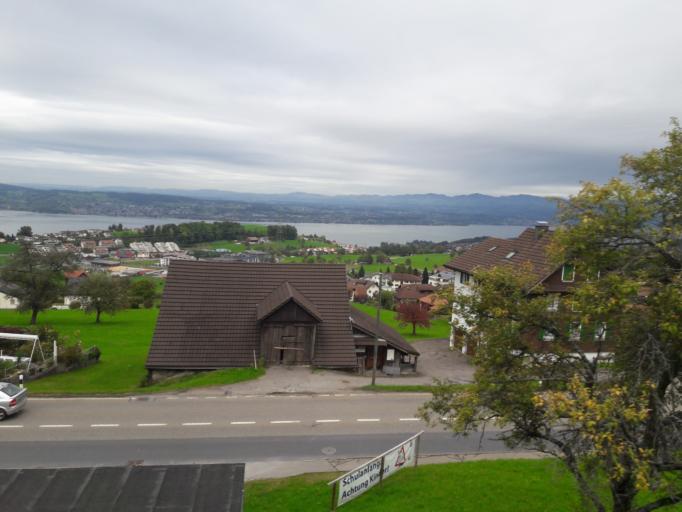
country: CH
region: Schwyz
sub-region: Bezirk Hoefe
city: Schindellegi
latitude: 47.1798
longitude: 8.7027
